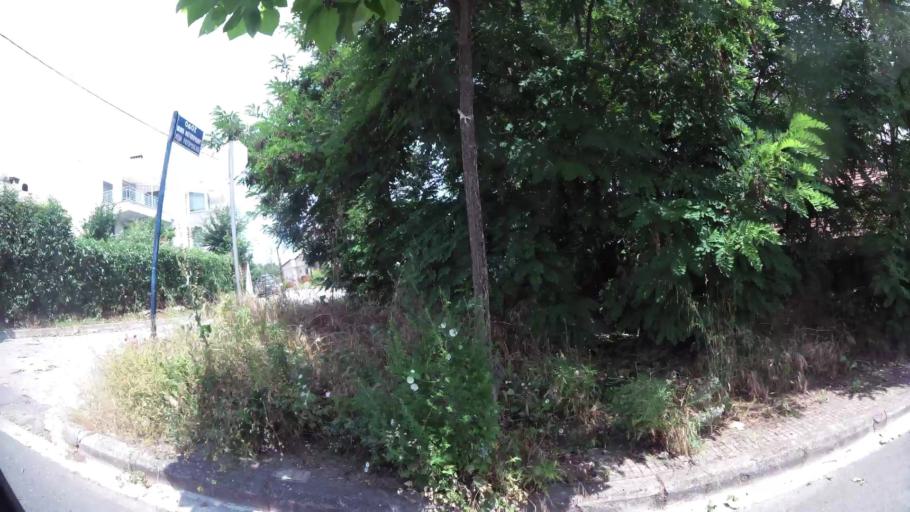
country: GR
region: West Macedonia
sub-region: Nomos Kozanis
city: Kozani
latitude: 40.3105
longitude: 21.7895
